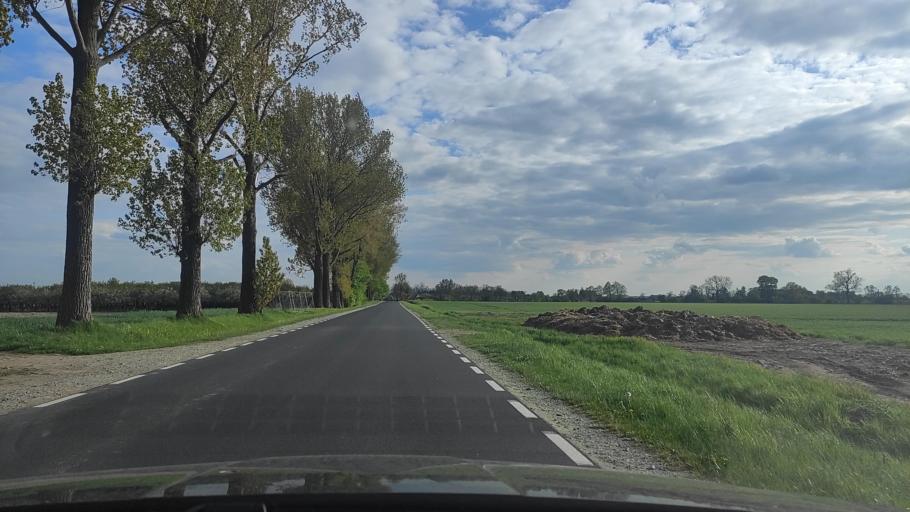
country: PL
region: Greater Poland Voivodeship
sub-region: Powiat poznanski
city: Kostrzyn
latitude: 52.4252
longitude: 17.2289
